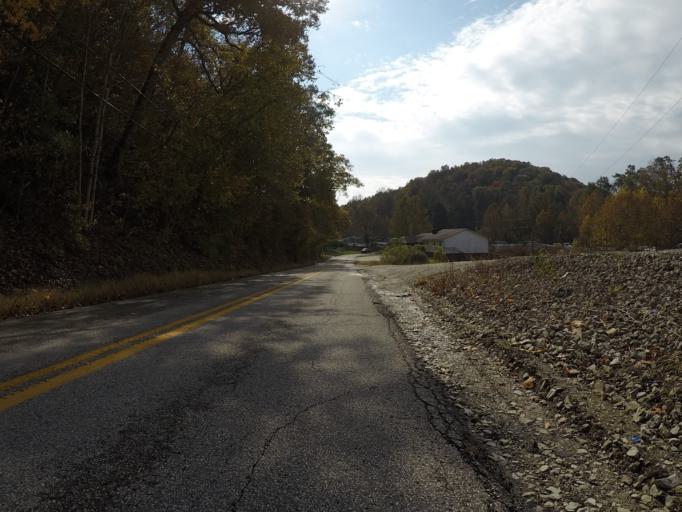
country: US
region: West Virginia
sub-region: Cabell County
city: Huntington
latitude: 38.3830
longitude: -82.3957
